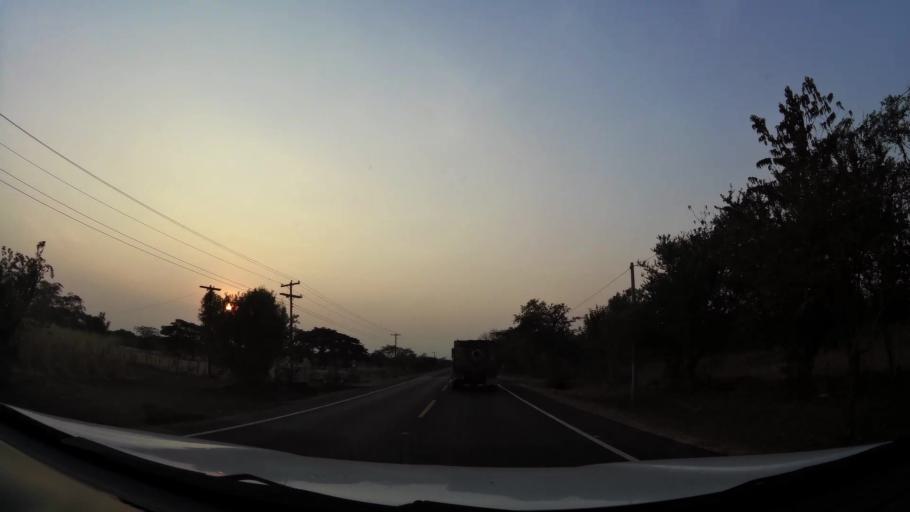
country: NI
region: Leon
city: La Paz Centro
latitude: 12.3149
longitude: -86.7883
